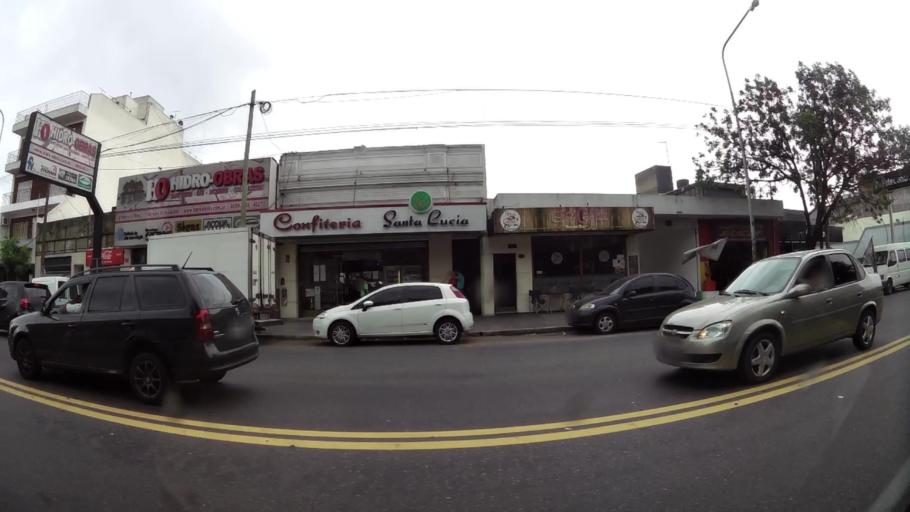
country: AR
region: Buenos Aires
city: San Justo
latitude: -34.6658
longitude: -58.5270
